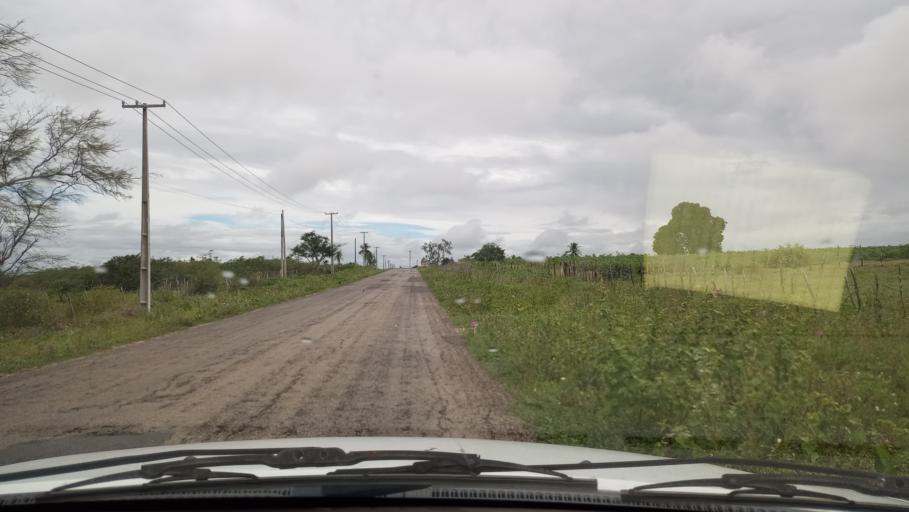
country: BR
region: Rio Grande do Norte
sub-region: Poco Branco
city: Poco Branco
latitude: -5.6144
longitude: -35.6485
